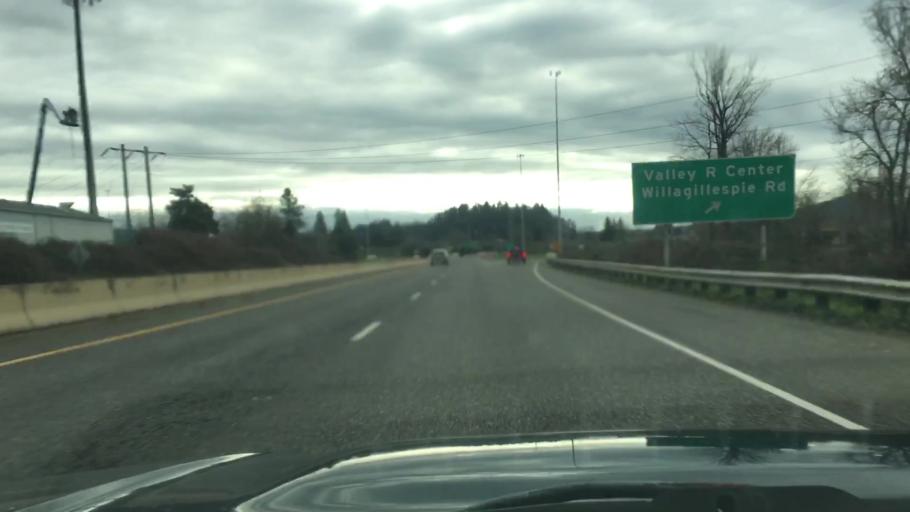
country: US
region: Oregon
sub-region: Lane County
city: Eugene
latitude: 44.0739
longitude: -123.1046
